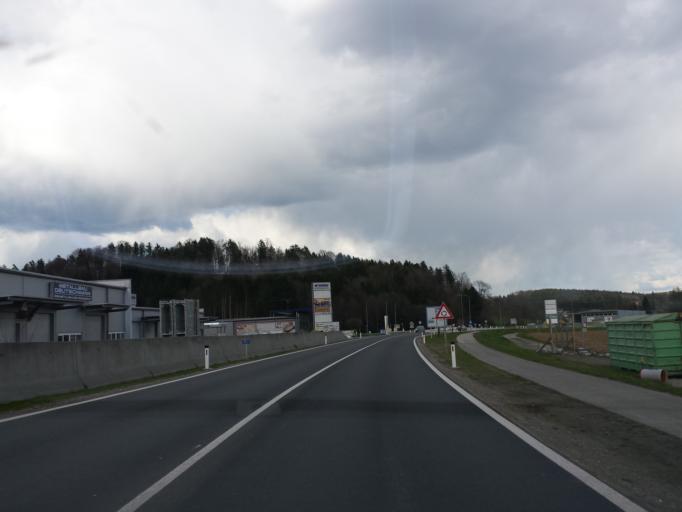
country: AT
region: Styria
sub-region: Politischer Bezirk Deutschlandsberg
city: Deutschlandsberg
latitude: 46.8297
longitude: 15.2392
